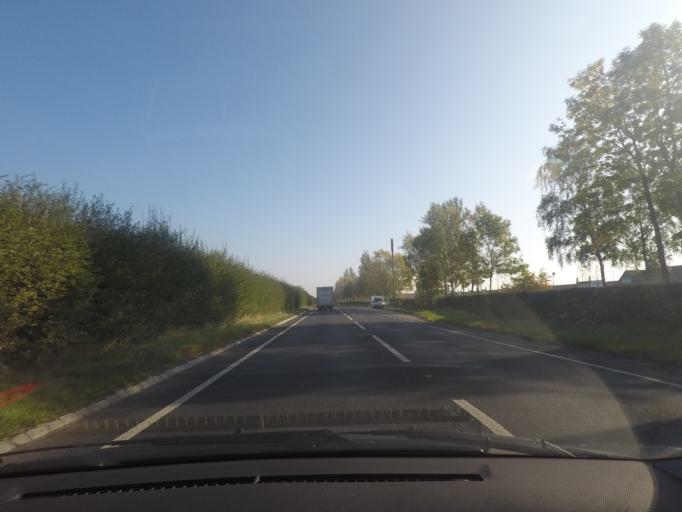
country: GB
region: England
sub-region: City of York
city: Wigginton
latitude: 53.9935
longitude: -1.1011
